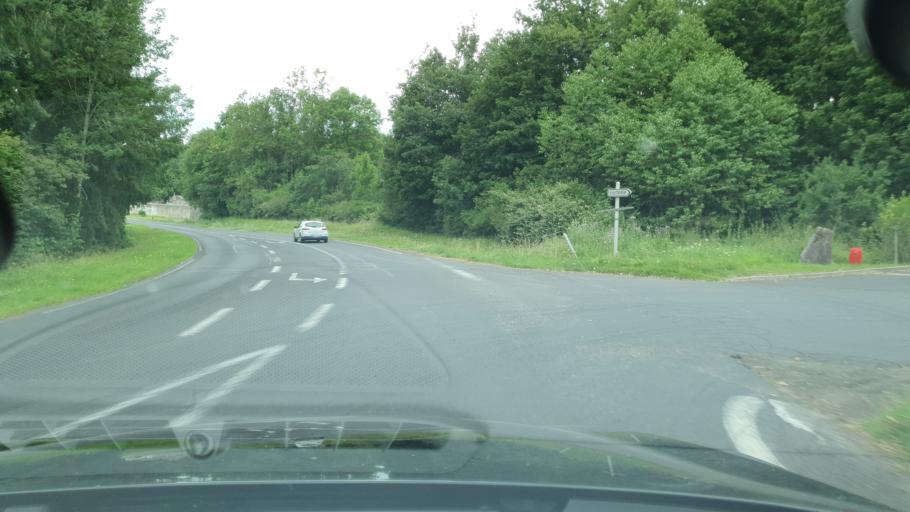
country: FR
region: Auvergne
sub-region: Departement du Puy-de-Dome
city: Aydat
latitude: 45.5745
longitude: 3.0200
